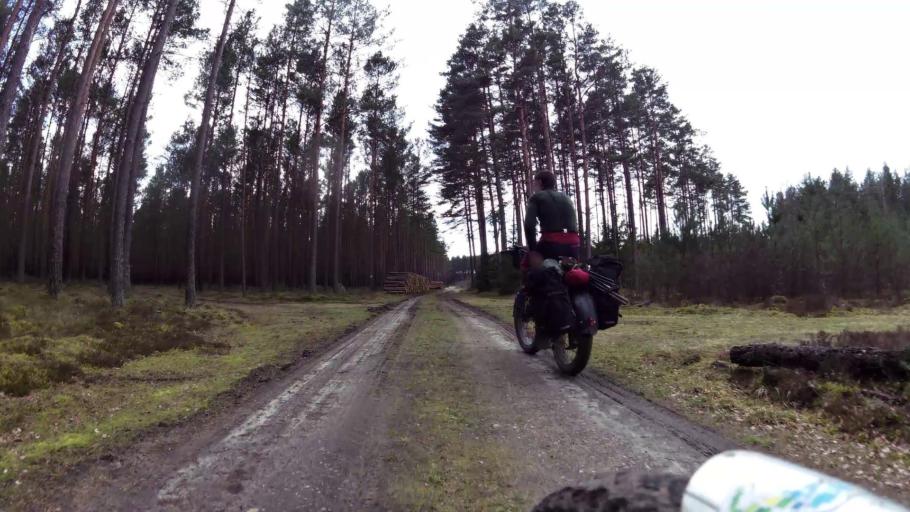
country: PL
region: Pomeranian Voivodeship
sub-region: Powiat bytowski
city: Kolczyglowy
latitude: 54.1681
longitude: 17.1965
